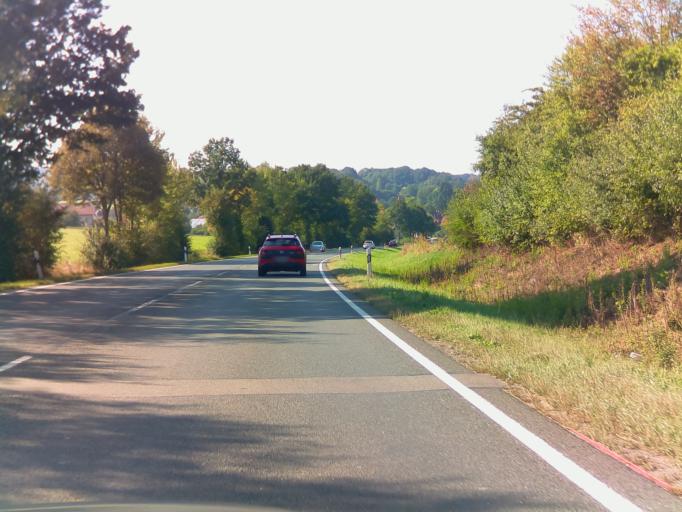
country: DE
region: Bavaria
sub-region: Upper Franconia
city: Hochstadt am Main
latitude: 50.1453
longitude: 11.1492
